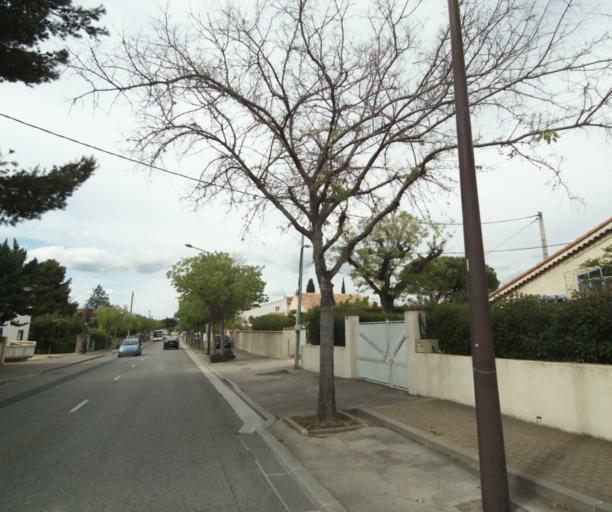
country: FR
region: Provence-Alpes-Cote d'Azur
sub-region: Departement des Bouches-du-Rhone
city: Rognac
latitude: 43.4900
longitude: 5.2298
